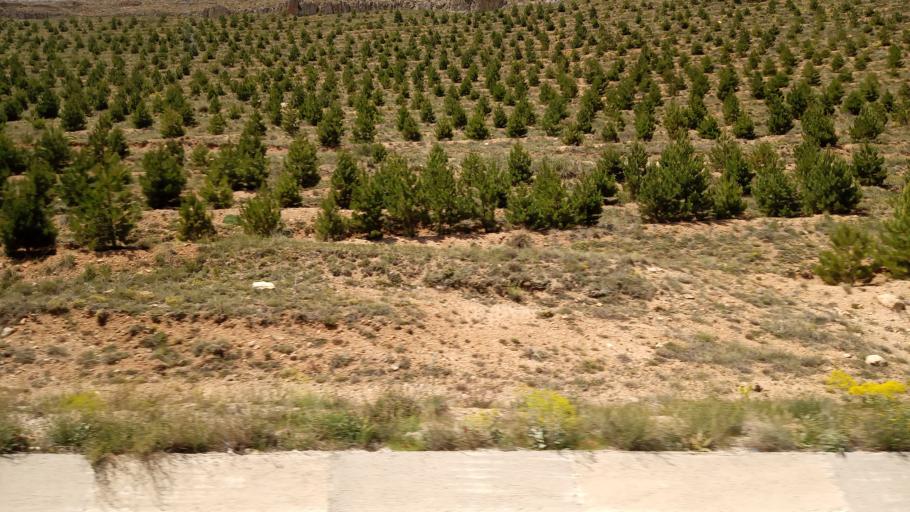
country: TR
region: Malatya
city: Darende
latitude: 38.6134
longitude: 37.4647
